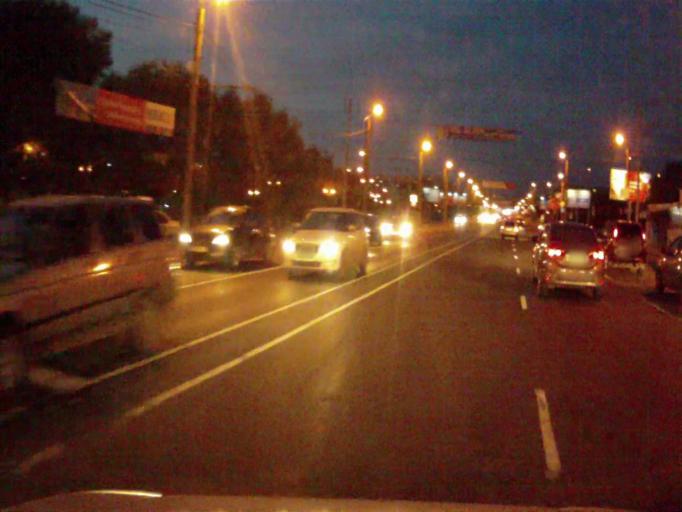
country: RU
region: Chelyabinsk
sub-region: Gorod Chelyabinsk
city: Chelyabinsk
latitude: 55.1712
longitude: 61.3582
